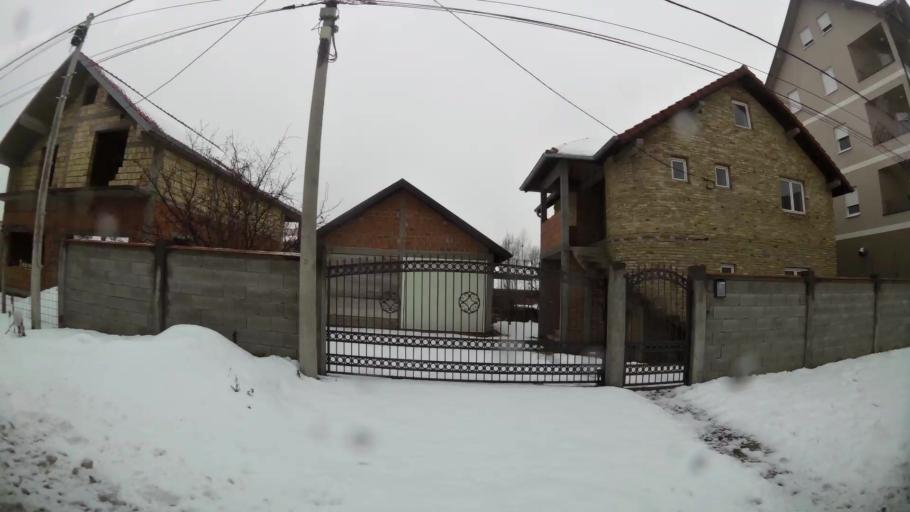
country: RS
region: Central Serbia
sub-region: Belgrade
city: Zemun
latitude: 44.8585
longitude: 20.3387
